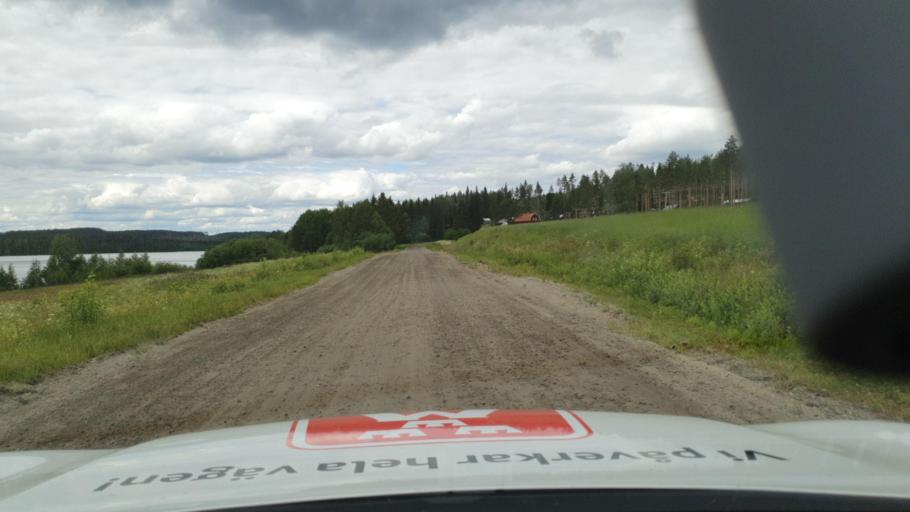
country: SE
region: Vaesterbotten
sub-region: Bjurholms Kommun
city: Bjurholm
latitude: 63.8307
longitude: 19.0088
